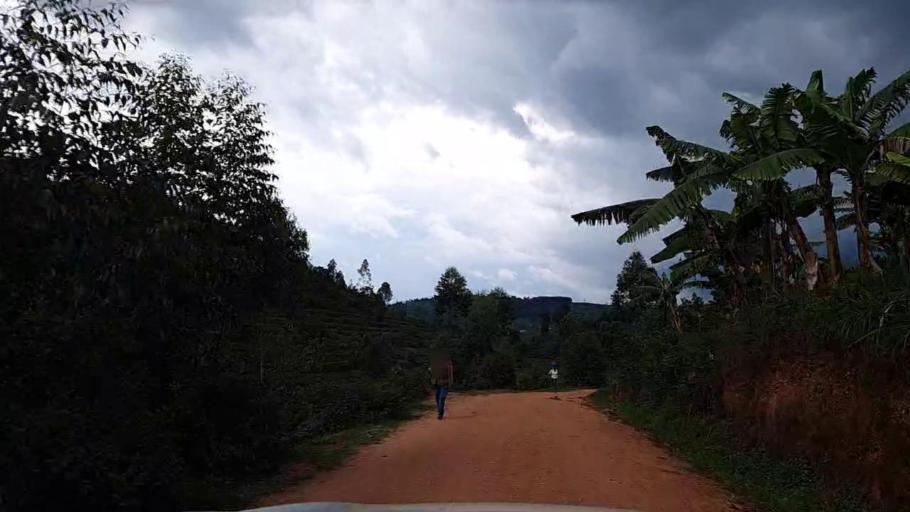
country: RW
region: Southern Province
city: Nyanza
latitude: -2.3922
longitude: 29.6897
